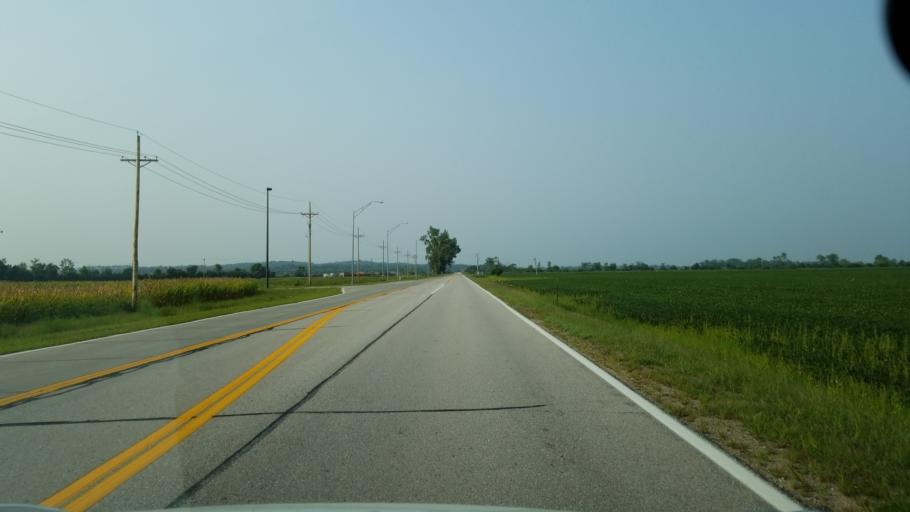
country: US
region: Nebraska
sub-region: Sarpy County
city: Bellevue
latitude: 41.1010
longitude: -95.8899
